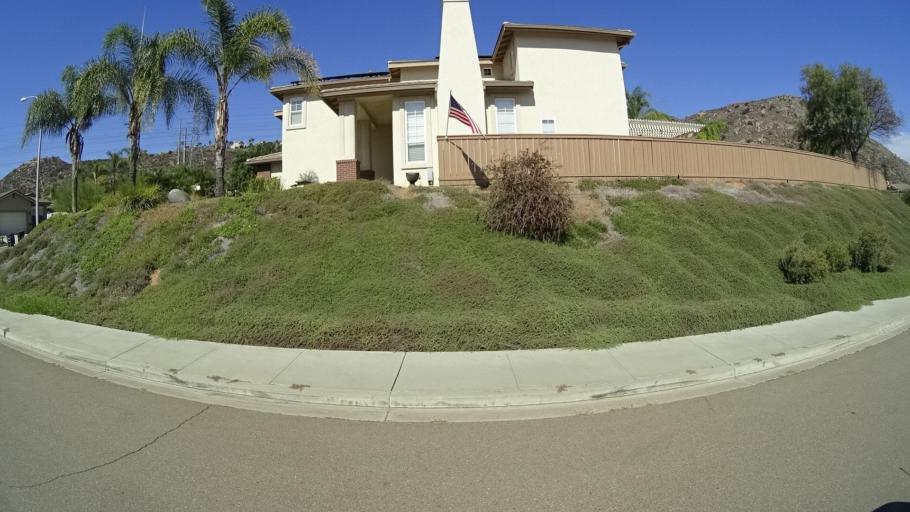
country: US
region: California
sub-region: San Diego County
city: Rancho San Diego
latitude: 32.7591
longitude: -116.9013
